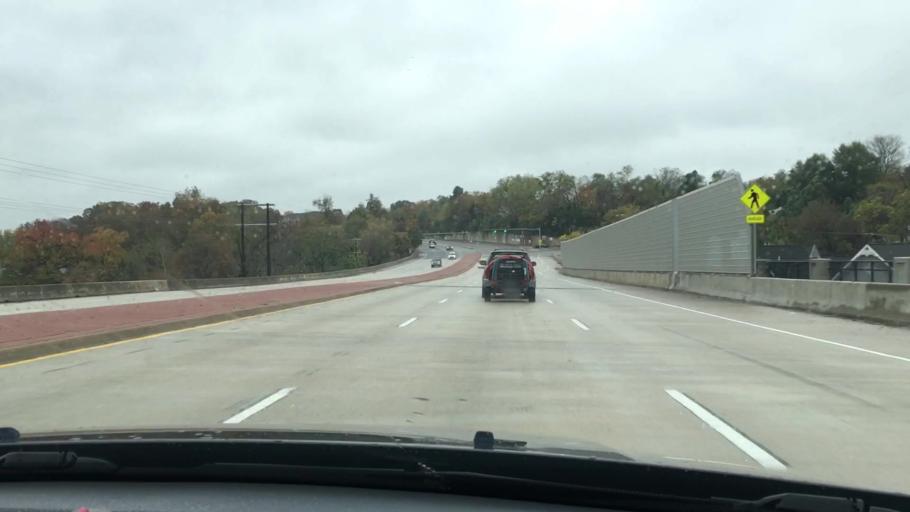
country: US
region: Virginia
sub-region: Prince William County
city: Woodbridge
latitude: 38.6838
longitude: -77.2583
